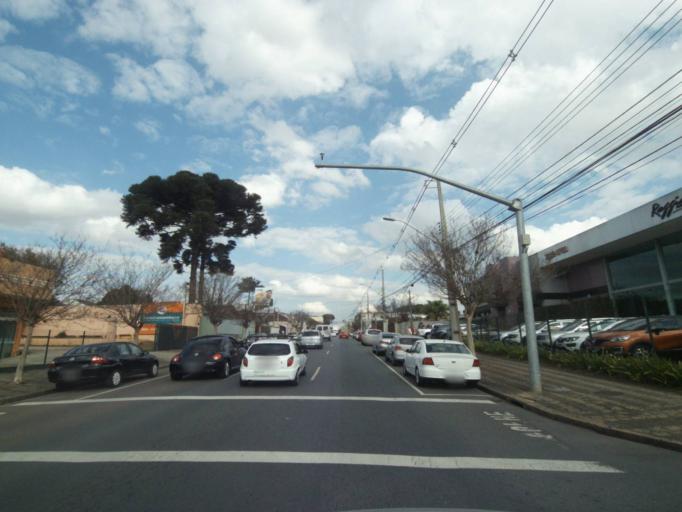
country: BR
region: Parana
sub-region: Curitiba
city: Curitiba
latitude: -25.4526
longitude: -49.2669
